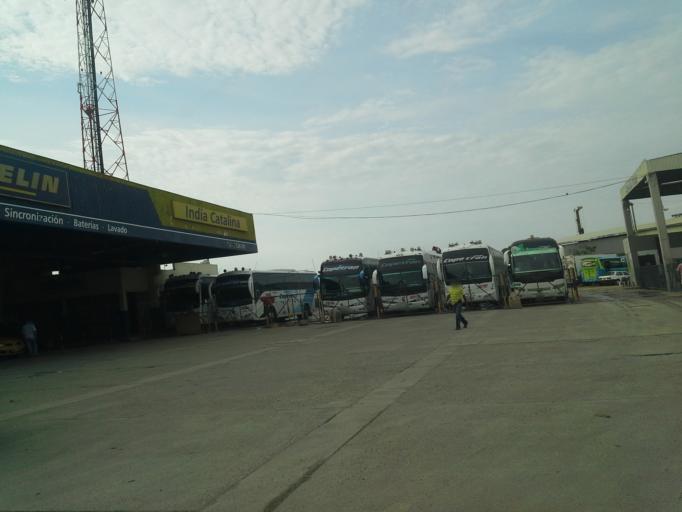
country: CO
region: Bolivar
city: Cartagena
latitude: 10.4017
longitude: -75.4622
